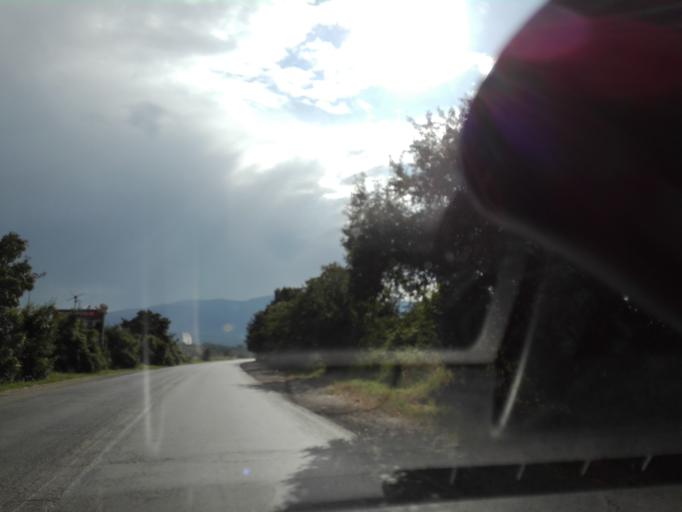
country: BG
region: Sofia-Capital
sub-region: Stolichna Obshtina
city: Sofia
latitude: 42.6230
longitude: 23.4417
